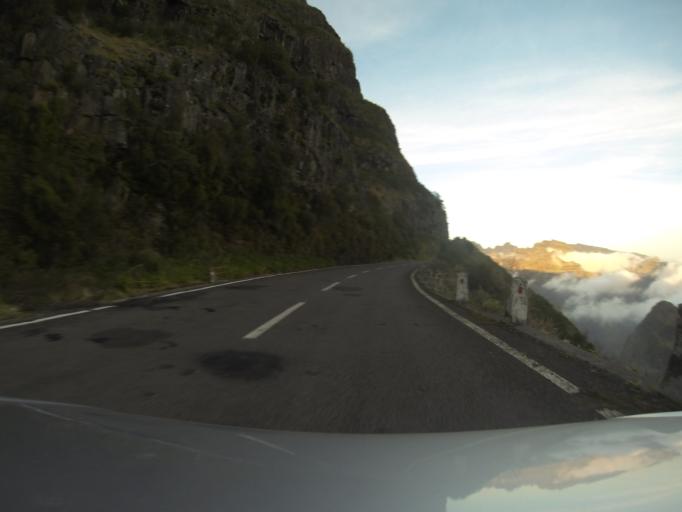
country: PT
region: Madeira
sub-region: Sao Vicente
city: Sao Vicente
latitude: 32.7404
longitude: -17.0480
